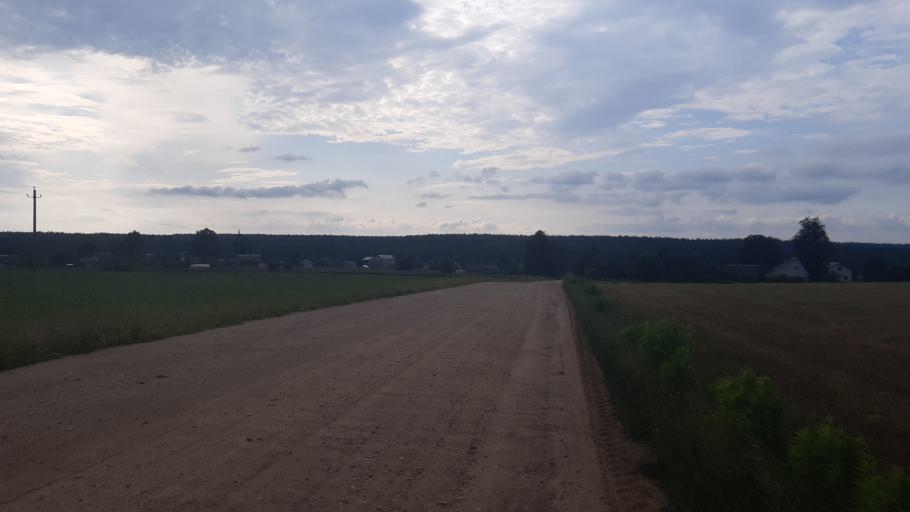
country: BY
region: Minsk
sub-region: Smalyavitski Rayon
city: Oktjabr'skij
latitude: 54.1254
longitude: 28.2050
